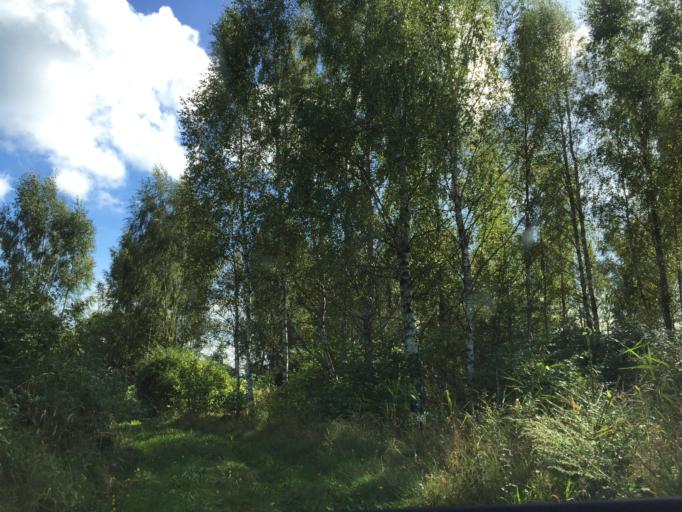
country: LV
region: Kuldigas Rajons
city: Kuldiga
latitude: 56.9973
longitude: 21.8200
